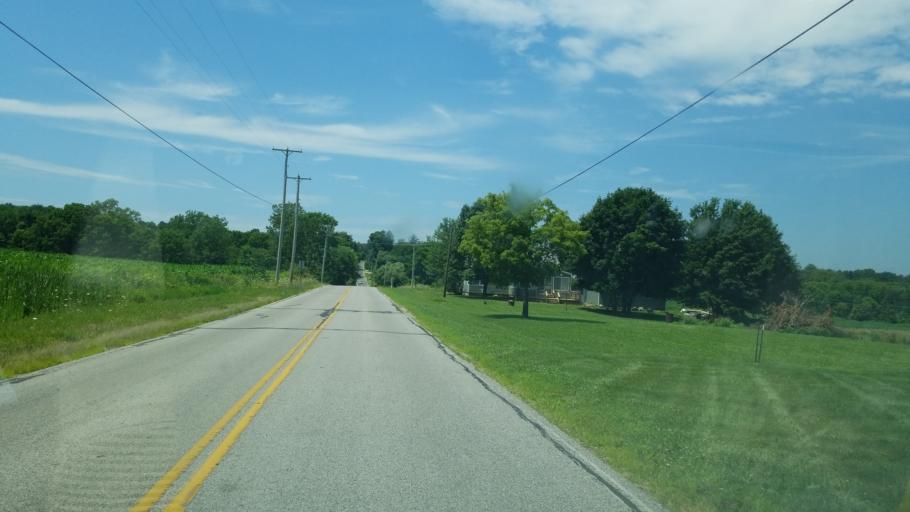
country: US
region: Ohio
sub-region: Ashland County
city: Ashland
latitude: 40.8925
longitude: -82.3421
